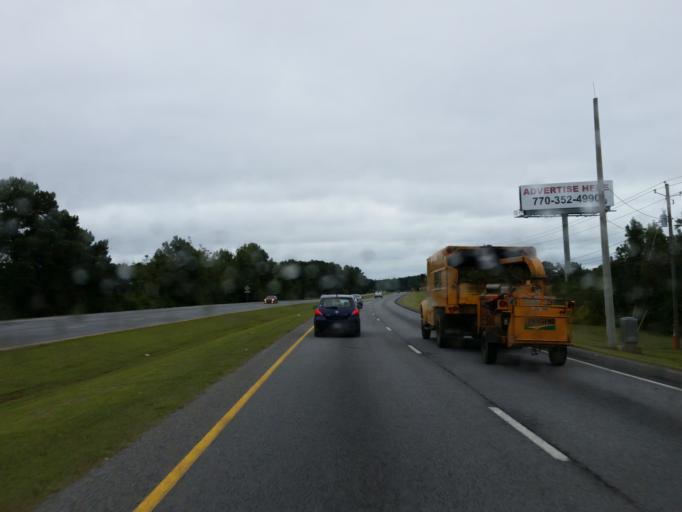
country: US
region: Georgia
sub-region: Clayton County
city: Lovejoy
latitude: 33.4388
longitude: -84.3210
